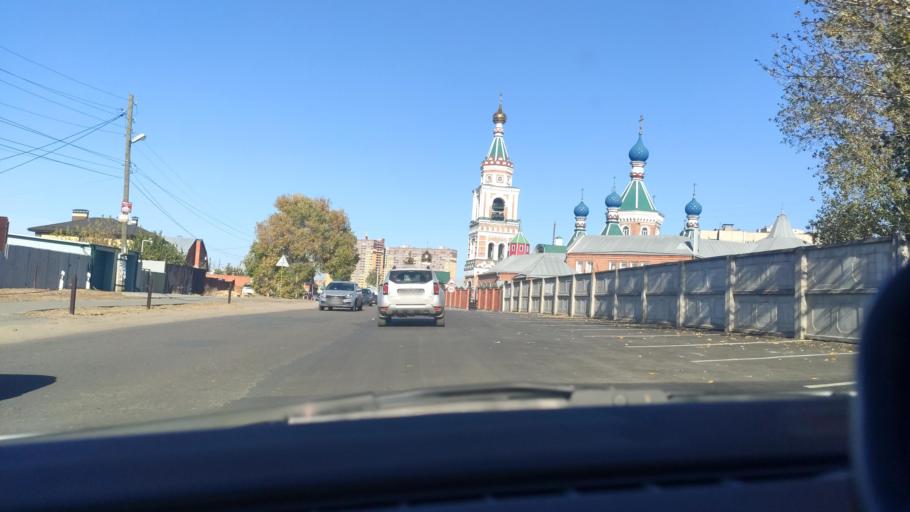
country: RU
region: Voronezj
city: Voronezh
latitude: 51.6990
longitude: 39.2680
